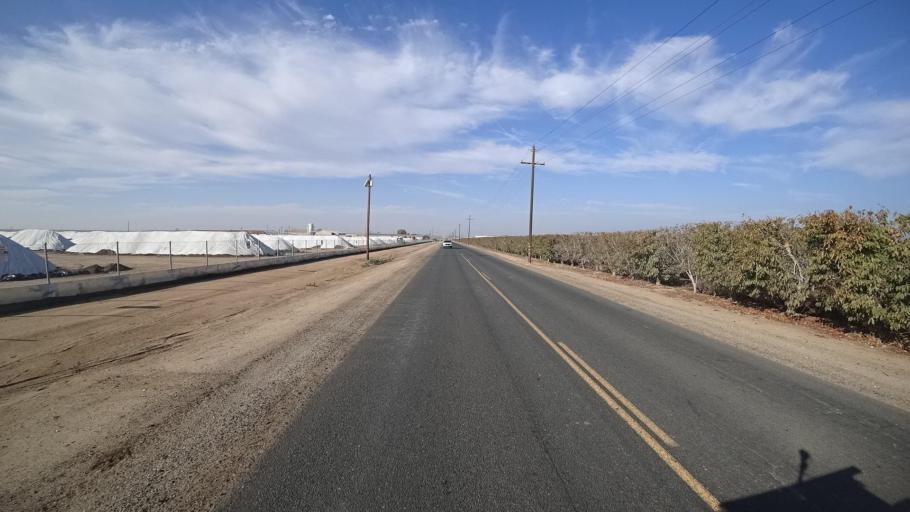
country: US
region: California
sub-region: Kern County
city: McFarland
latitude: 35.6020
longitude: -119.1872
